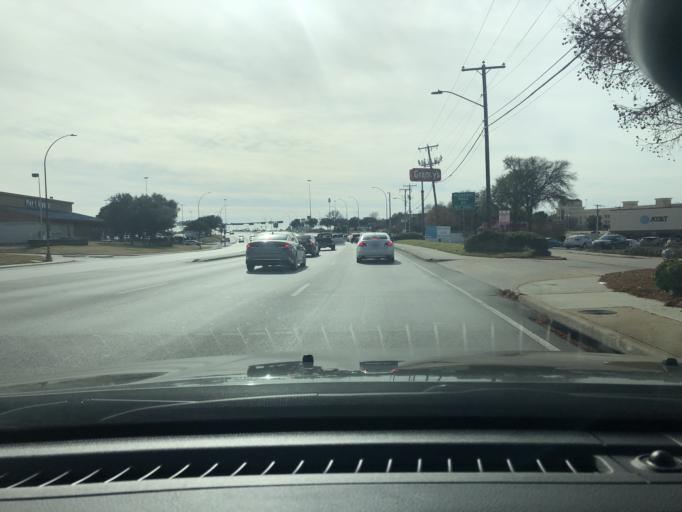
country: US
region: Texas
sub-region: Tarrant County
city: Dalworthington Gardens
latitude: 32.6807
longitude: -97.1346
